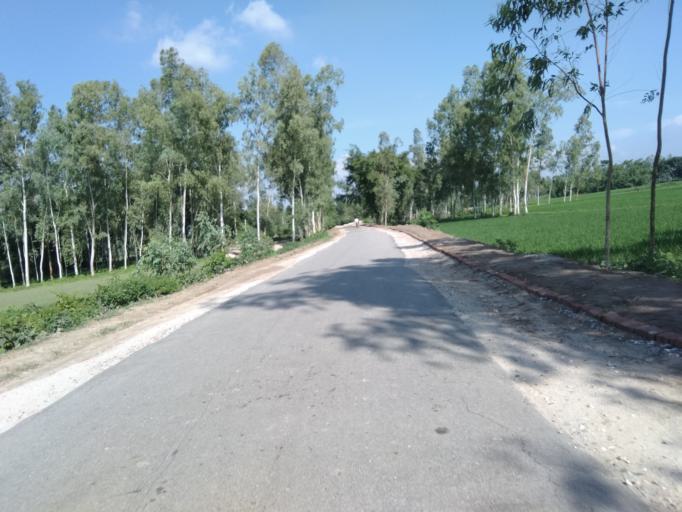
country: BD
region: Rangpur Division
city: Panchagarh
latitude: 26.2554
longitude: 88.6206
